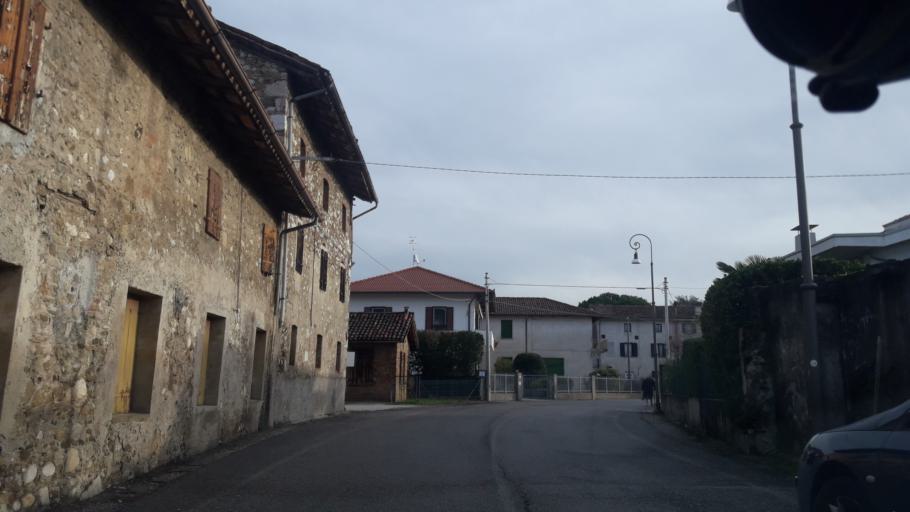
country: IT
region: Friuli Venezia Giulia
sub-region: Provincia di Udine
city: Colugna
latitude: 46.0850
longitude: 13.2048
